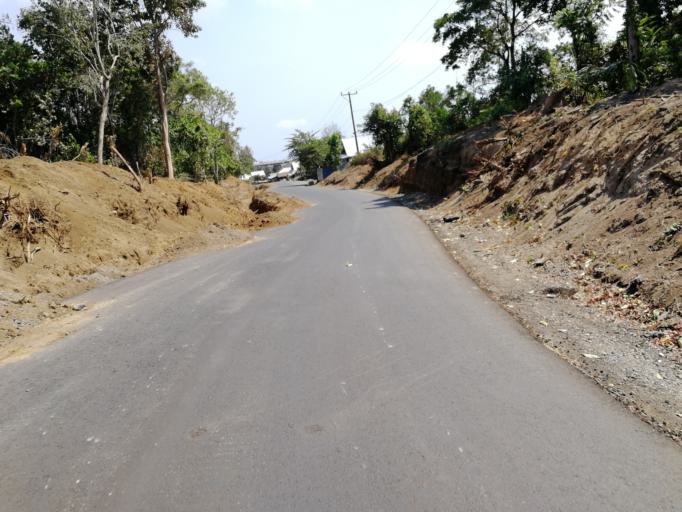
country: ID
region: West Nusa Tenggara
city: Lelongken
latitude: -8.3246
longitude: 116.4960
